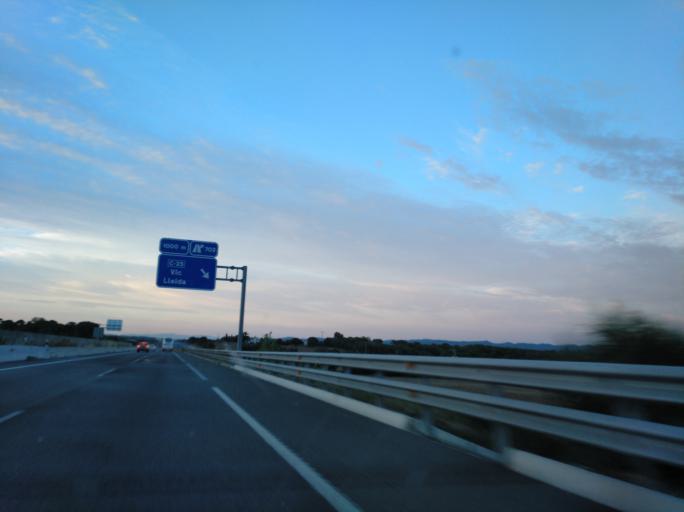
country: ES
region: Catalonia
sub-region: Provincia de Girona
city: Vilobi d'Onyar
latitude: 41.8581
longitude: 2.7749
